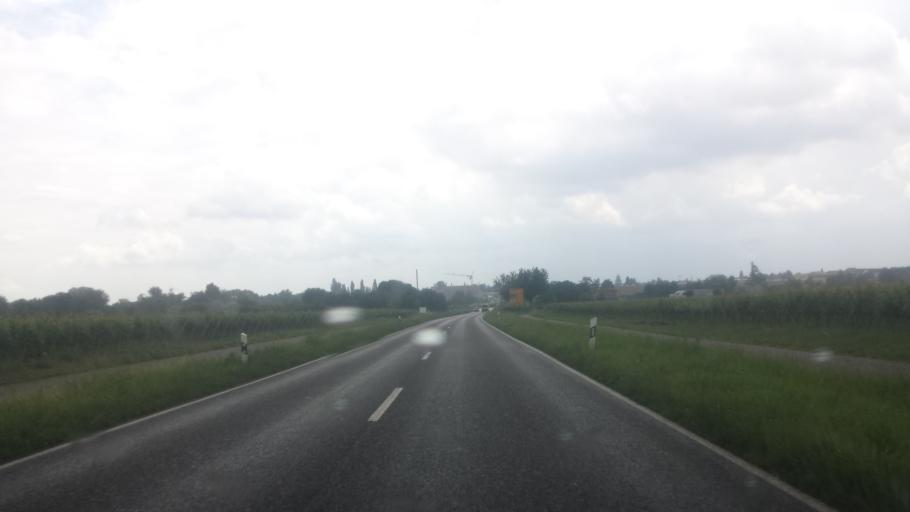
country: DE
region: Rheinland-Pfalz
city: Maikammer
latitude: 49.2937
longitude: 8.1405
